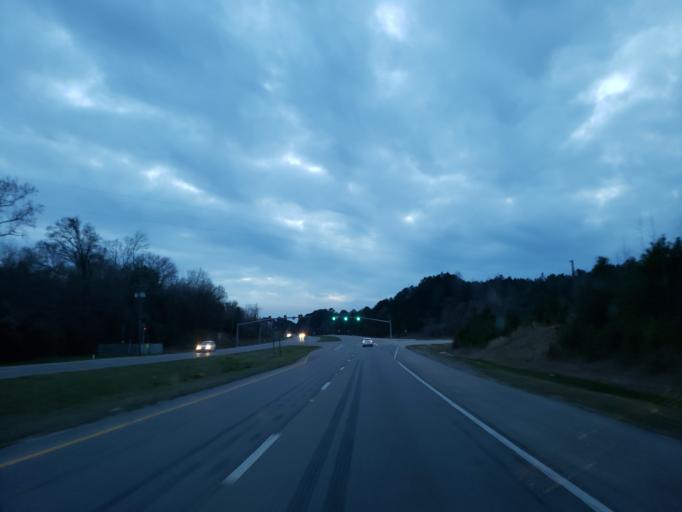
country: US
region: Mississippi
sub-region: Lauderdale County
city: Marion
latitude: 32.3666
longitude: -88.6518
